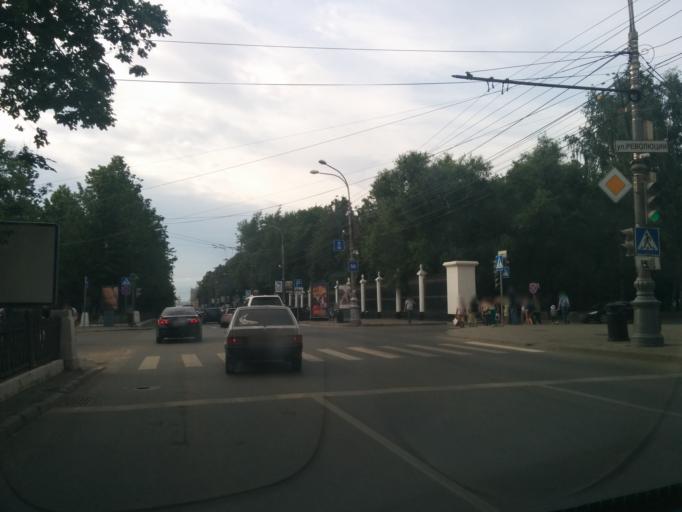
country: RU
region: Perm
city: Perm
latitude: 58.0023
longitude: 56.2477
